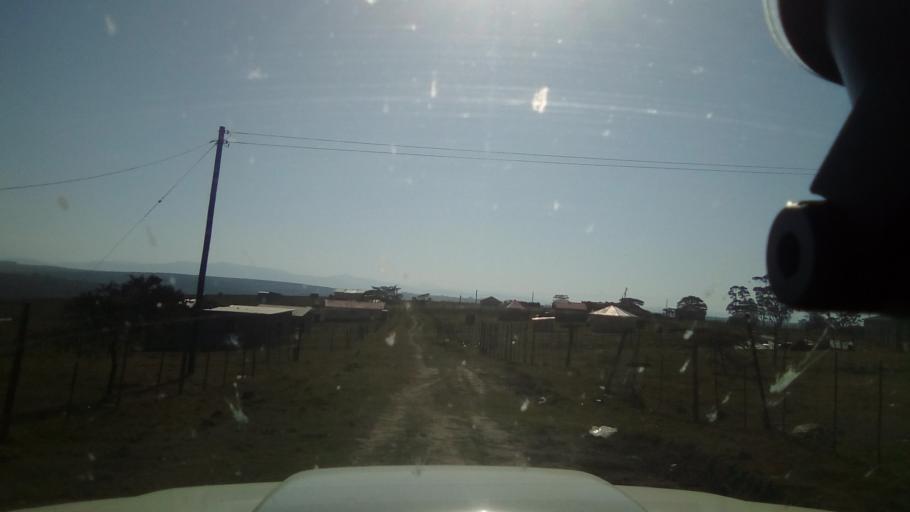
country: ZA
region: Eastern Cape
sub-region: Buffalo City Metropolitan Municipality
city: Bhisho
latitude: -32.9354
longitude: 27.3352
